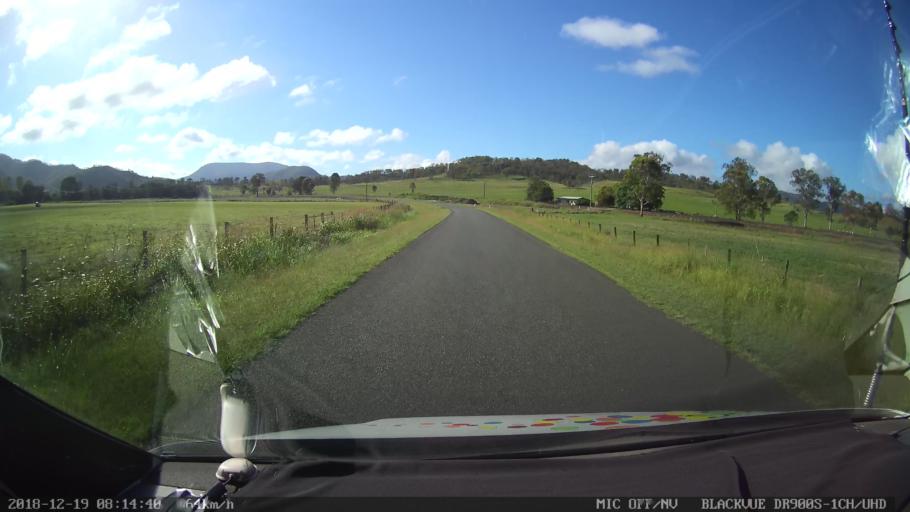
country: AU
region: Queensland
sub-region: Logan
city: Cedar Vale
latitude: -28.2493
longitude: 152.8920
